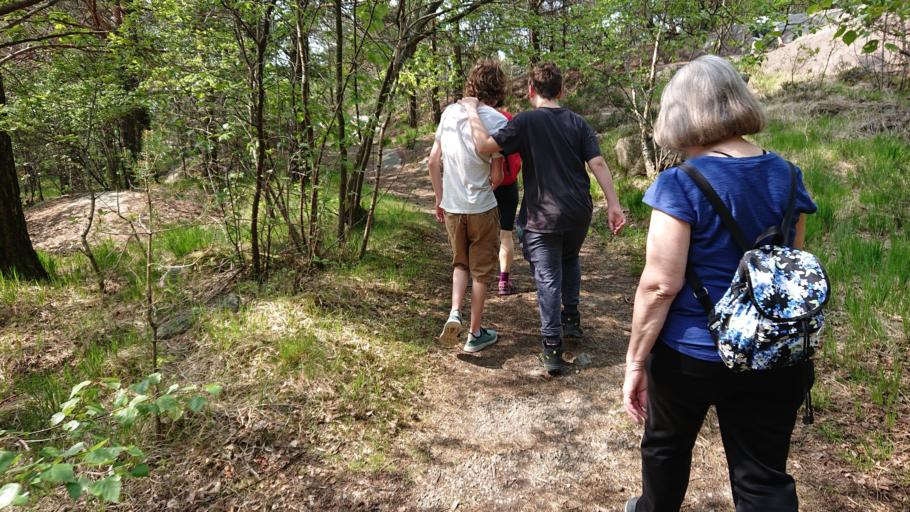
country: NO
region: Rogaland
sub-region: Sandnes
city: Sandnes
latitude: 58.9025
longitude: 5.7769
